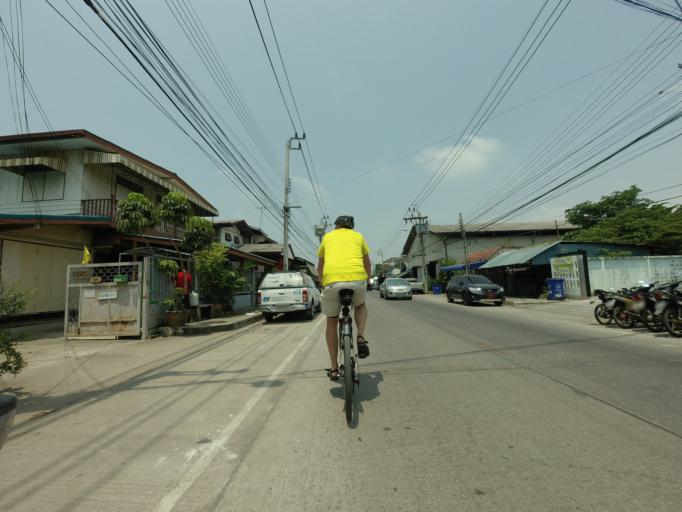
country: TH
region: Samut Prakan
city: Phra Samut Chedi
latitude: 13.5721
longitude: 100.5723
